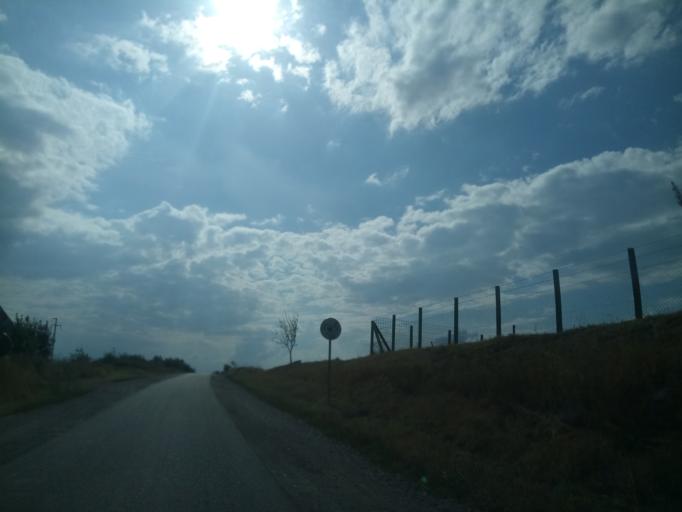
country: RS
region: Autonomna Pokrajina Vojvodina
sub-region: Sremski Okrug
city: Irig
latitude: 45.1020
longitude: 19.8998
